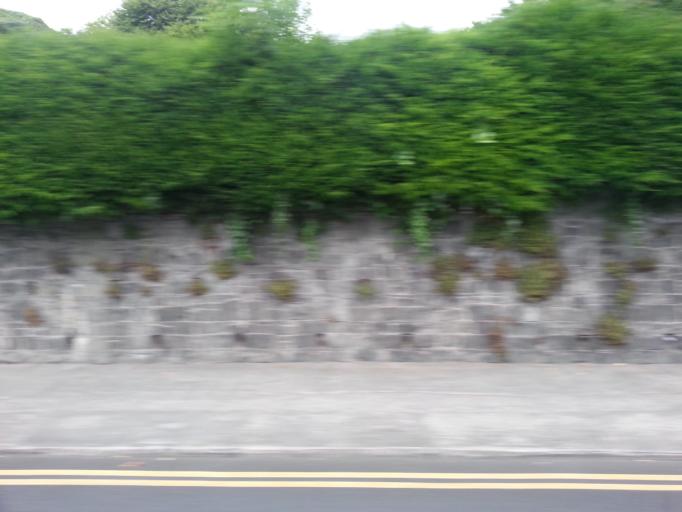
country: IE
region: Leinster
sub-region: Kilkenny
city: Kilkenny
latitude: 52.6529
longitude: -7.2419
